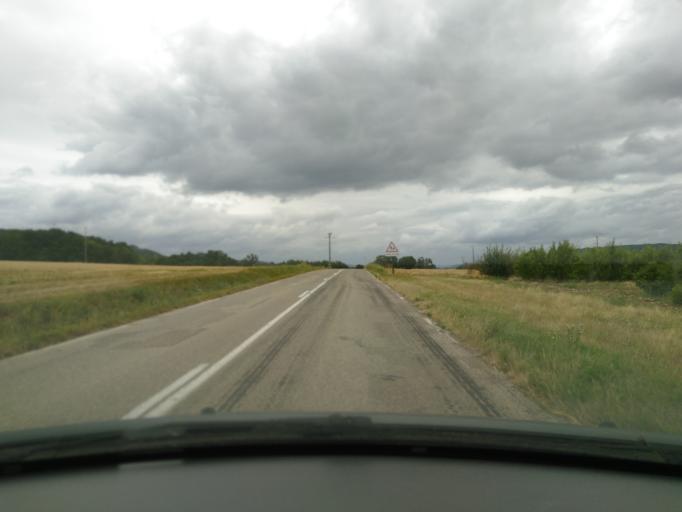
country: FR
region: Rhone-Alpes
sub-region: Departement de l'Isere
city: La Cote-Saint-Andre
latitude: 45.4298
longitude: 5.2430
